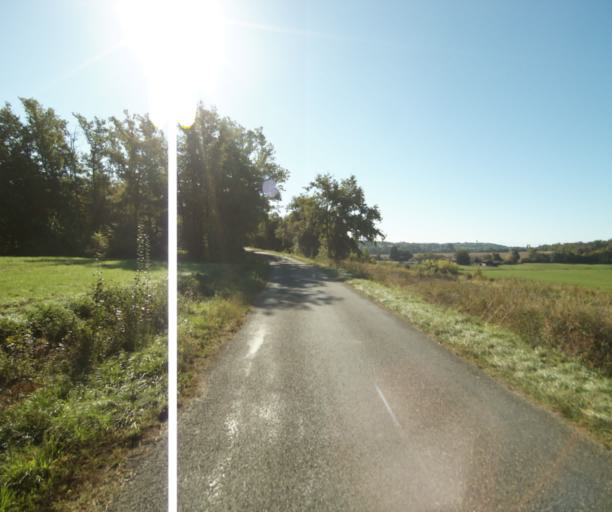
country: FR
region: Midi-Pyrenees
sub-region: Departement du Gers
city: Gondrin
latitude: 43.8173
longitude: 0.2202
